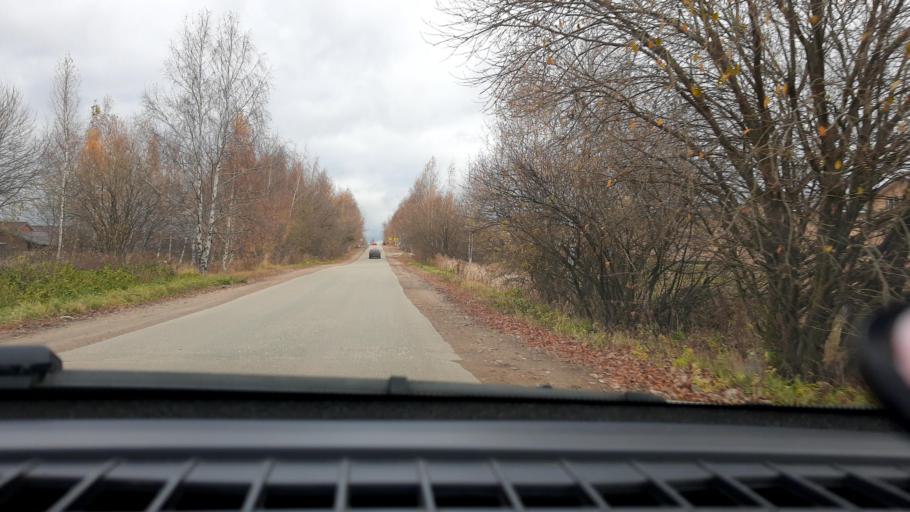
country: RU
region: Nizjnij Novgorod
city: Afonino
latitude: 56.2018
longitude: 44.1353
